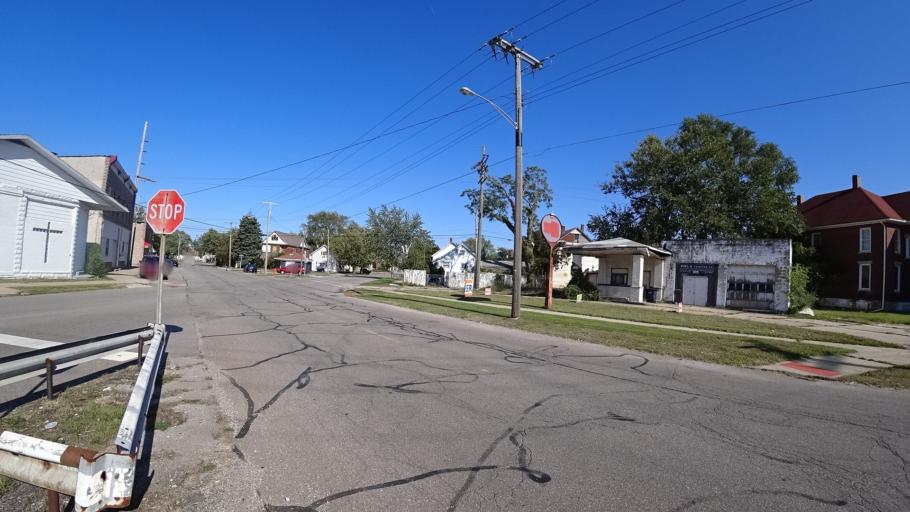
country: US
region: Indiana
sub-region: LaPorte County
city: Michigan City
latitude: 41.7095
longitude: -86.9082
